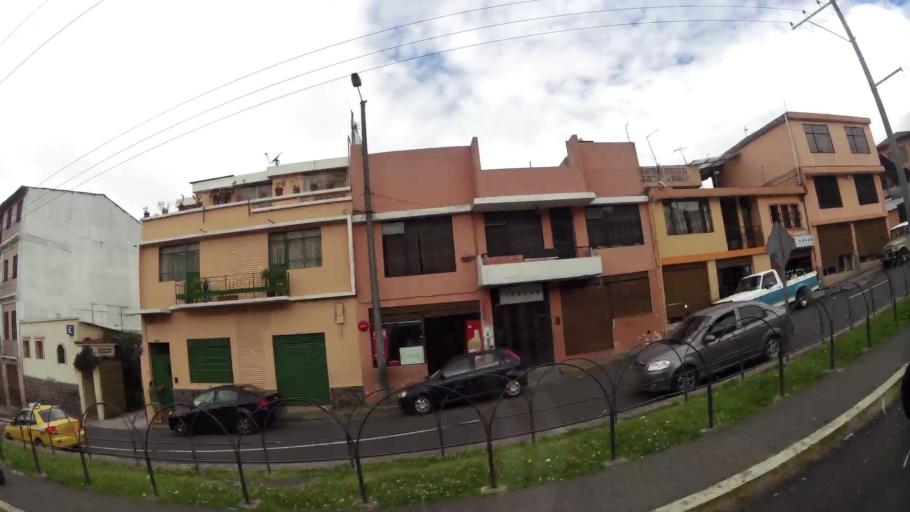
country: EC
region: Pichincha
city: Quito
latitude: -0.2242
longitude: -78.5101
